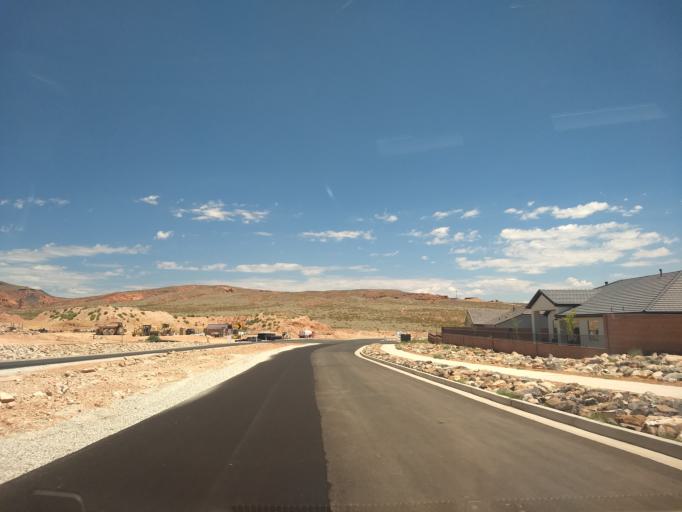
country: US
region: Utah
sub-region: Washington County
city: Washington
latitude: 37.1594
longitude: -113.5232
